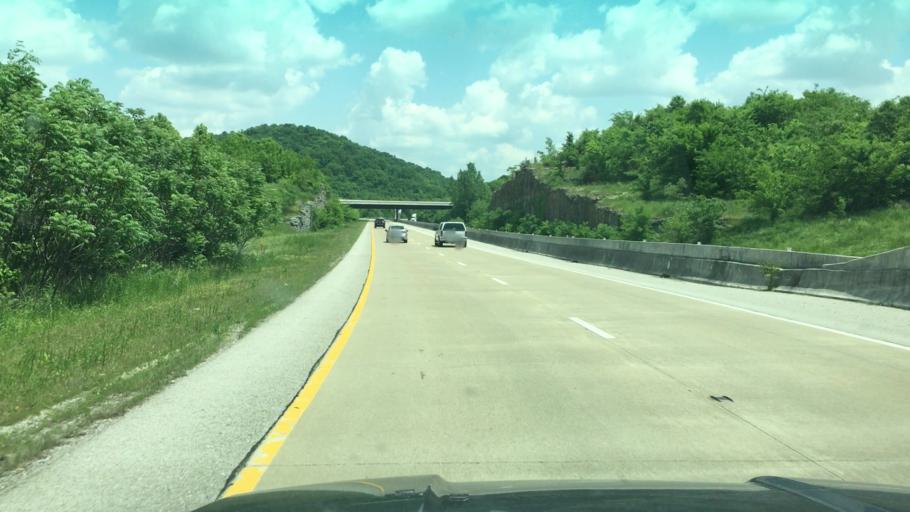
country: US
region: Tennessee
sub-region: Williamson County
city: Thompson's Station
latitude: 35.8195
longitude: -86.8385
